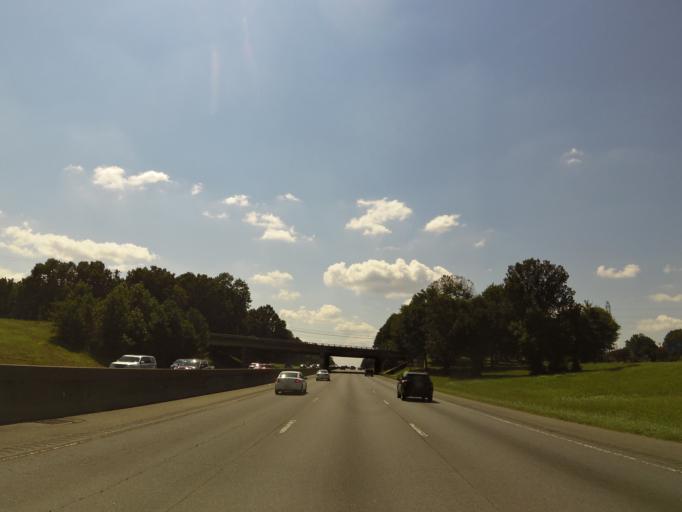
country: US
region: North Carolina
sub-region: Gaston County
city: Lowell
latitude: 35.2641
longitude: -81.0871
